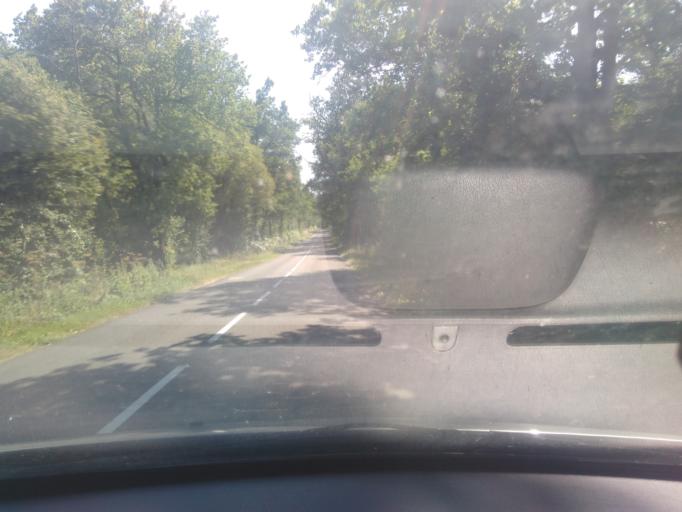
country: FR
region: Pays de la Loire
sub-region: Departement de la Vendee
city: La Ferriere
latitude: 46.6909
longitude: -1.3430
